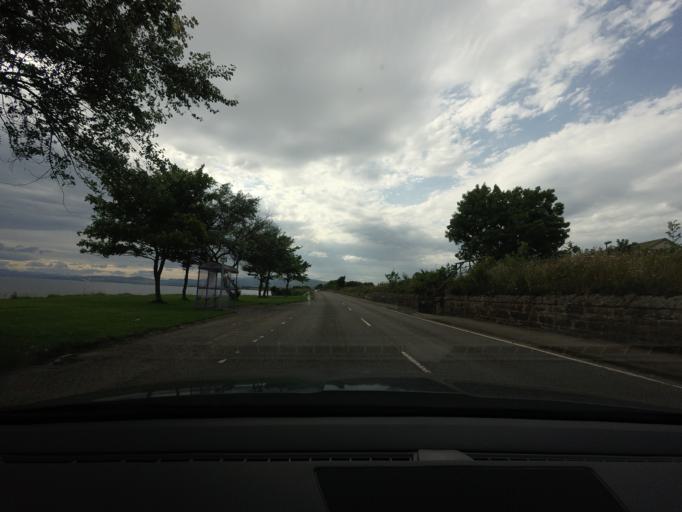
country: GB
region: Scotland
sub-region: Highland
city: Invergordon
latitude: 57.6912
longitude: -4.1887
